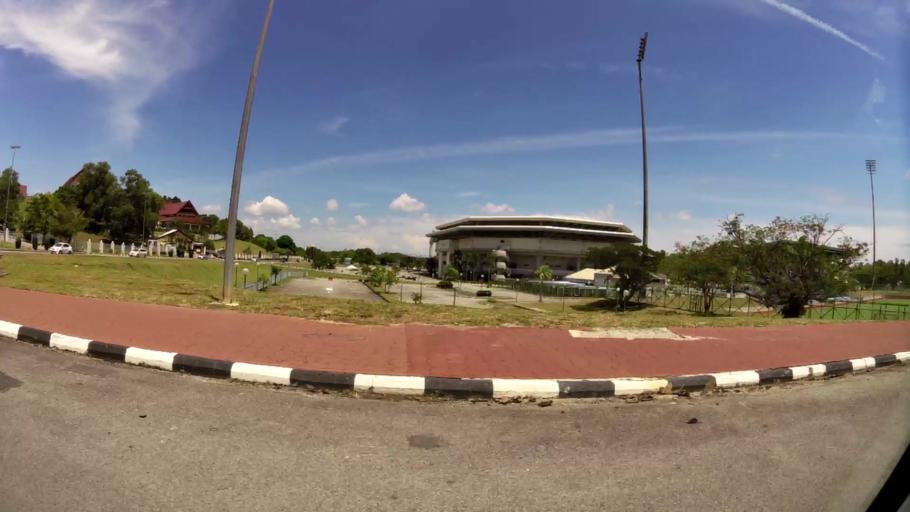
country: BN
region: Brunei and Muara
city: Bandar Seri Begawan
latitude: 4.9268
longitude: 114.9509
